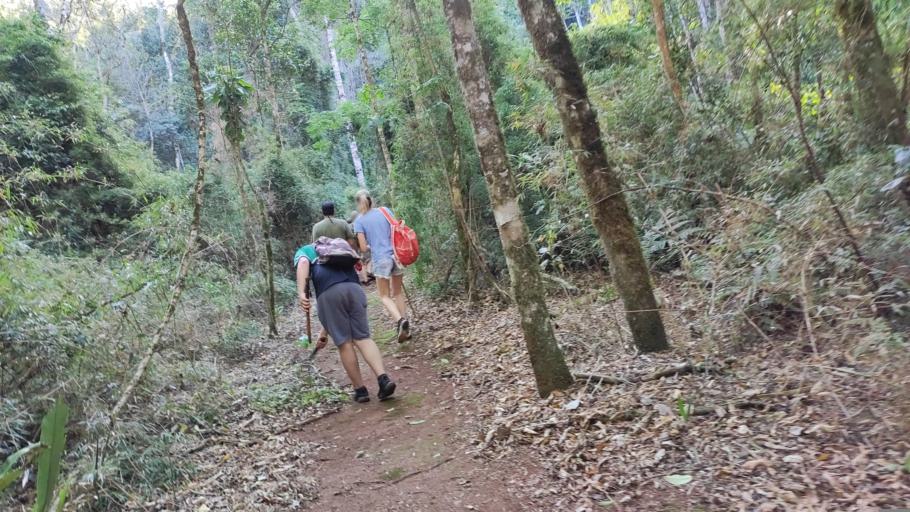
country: AR
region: Misiones
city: Dos de Mayo
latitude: -26.9937
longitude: -54.6327
